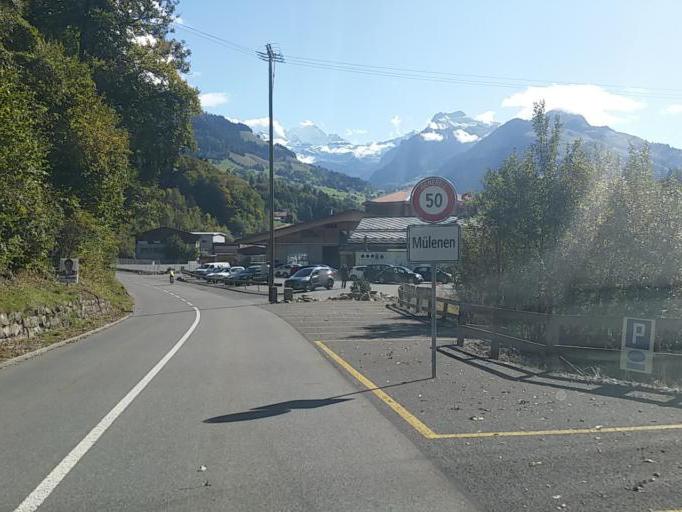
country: CH
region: Bern
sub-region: Frutigen-Niedersimmental District
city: Aeschi
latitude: 46.6463
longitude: 7.6901
